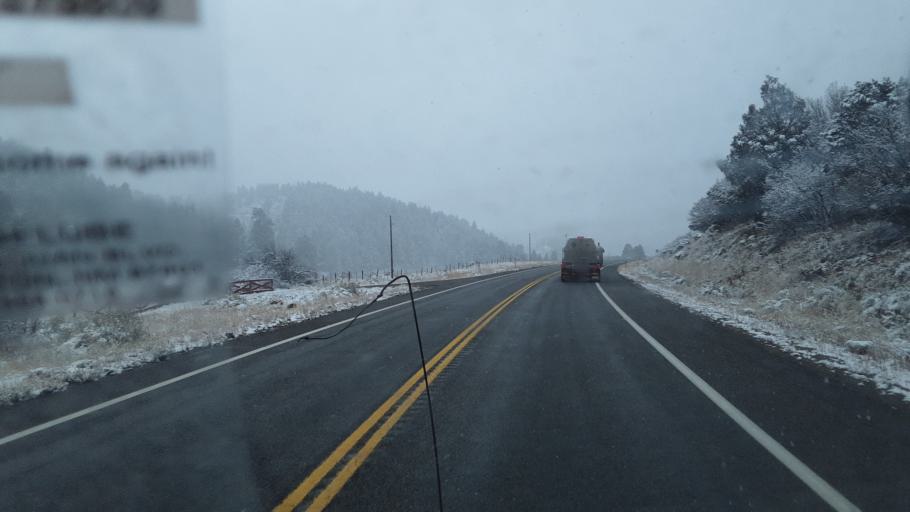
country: US
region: Colorado
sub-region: La Plata County
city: Bayfield
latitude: 37.2292
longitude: -107.3859
